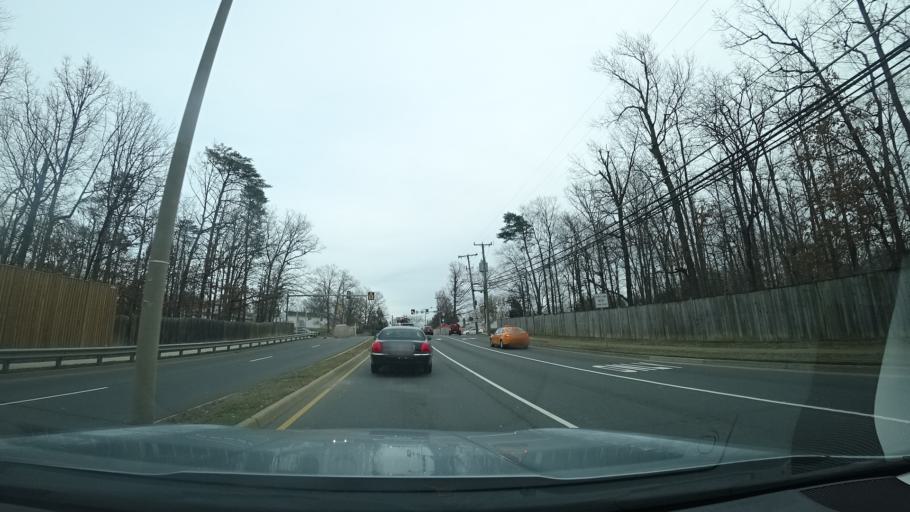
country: US
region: Virginia
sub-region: Loudoun County
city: Oak Grove
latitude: 38.9753
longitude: -77.4053
